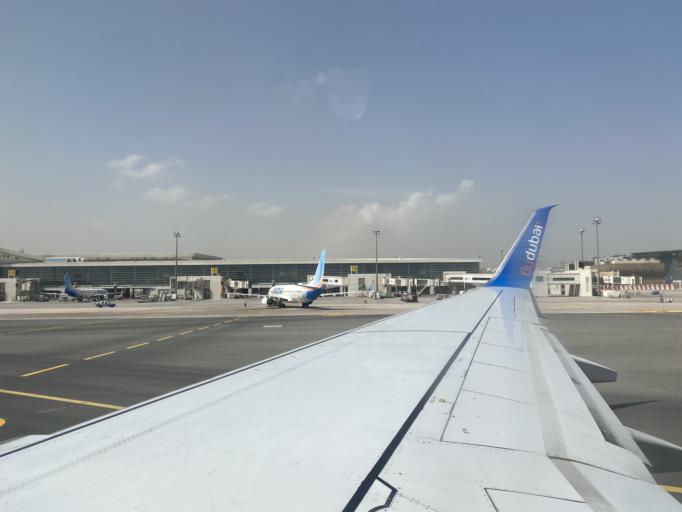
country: AE
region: Ash Shariqah
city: Sharjah
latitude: 25.2617
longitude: 55.3434
